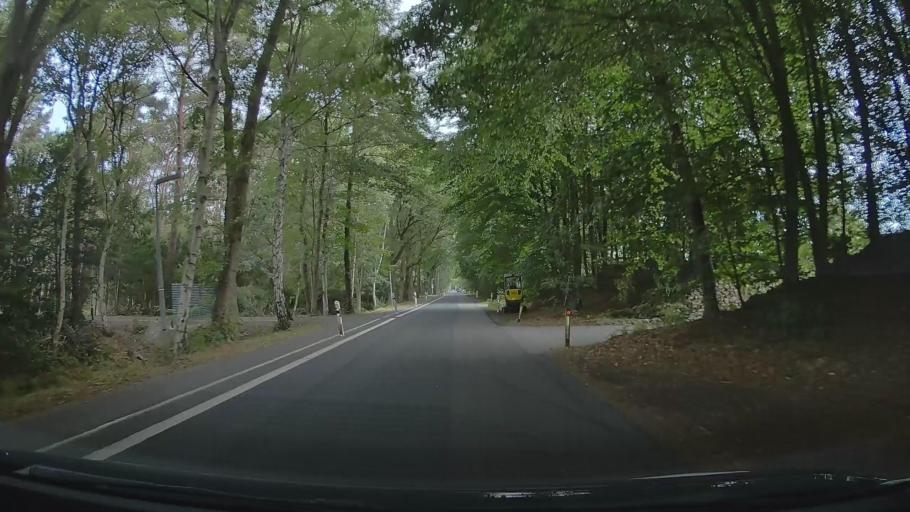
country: DE
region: Lower Saxony
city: Wardenburg
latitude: 53.1085
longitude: 8.1129
